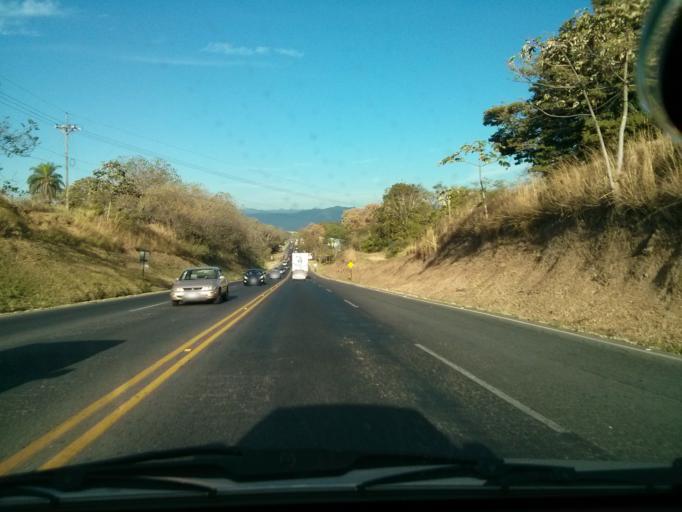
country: CR
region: Alajuela
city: Carrillos
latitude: 10.0014
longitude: -84.2839
